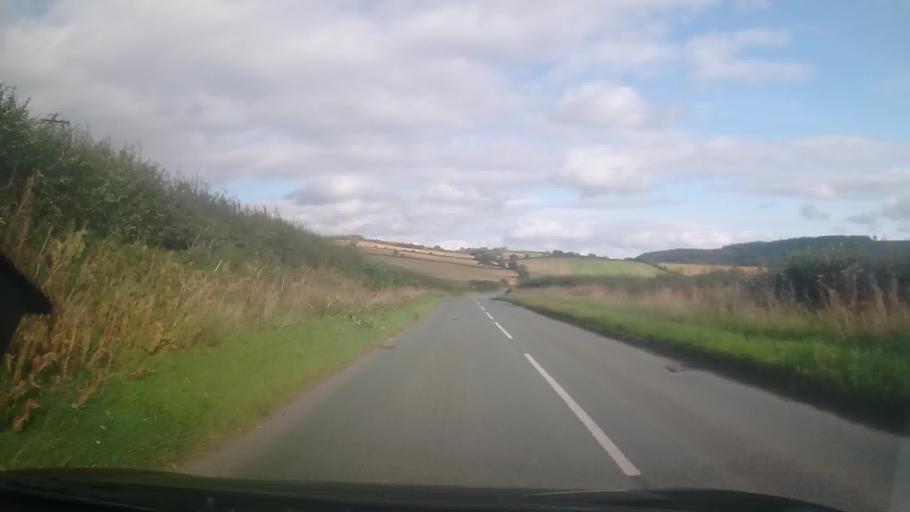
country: GB
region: England
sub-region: Shropshire
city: Lydham
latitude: 52.4680
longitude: -2.9417
